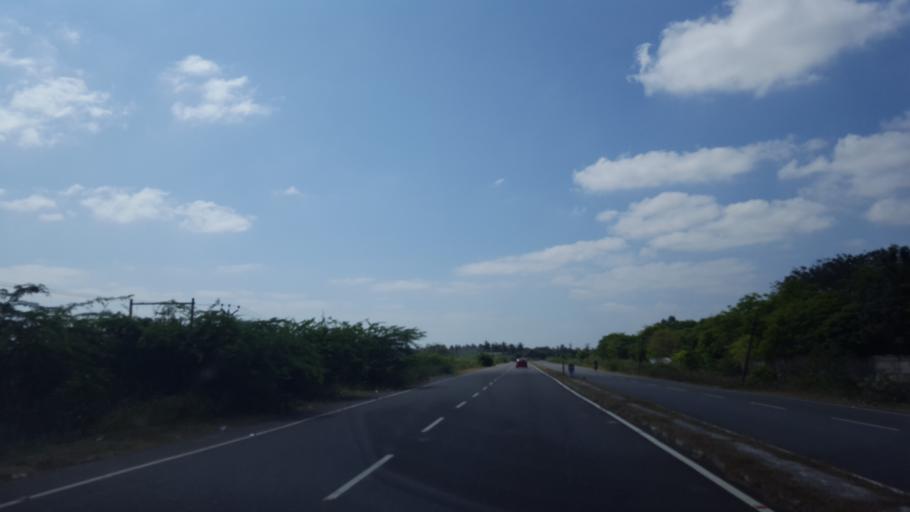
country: IN
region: Tamil Nadu
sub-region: Kancheepuram
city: Mamallapuram
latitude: 12.6550
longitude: 80.1761
